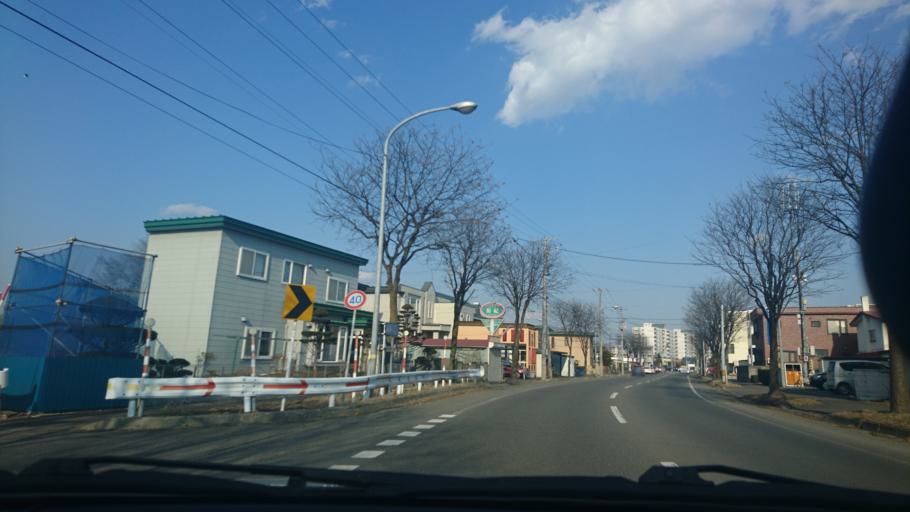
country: JP
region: Hokkaido
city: Obihiro
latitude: 42.9253
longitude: 143.1616
